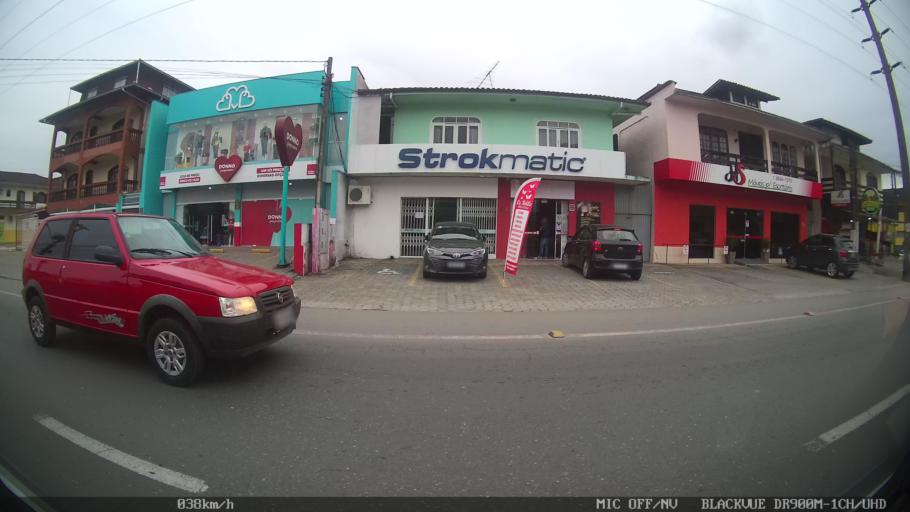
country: BR
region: Santa Catarina
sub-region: Joinville
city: Joinville
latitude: -26.2773
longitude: -48.8215
